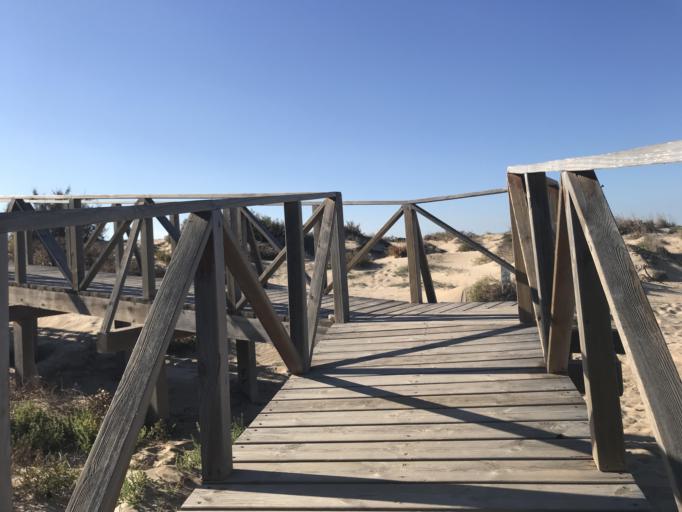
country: ES
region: Valencia
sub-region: Provincia de Alicante
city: Guardamar del Segura
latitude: 38.0324
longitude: -0.6515
